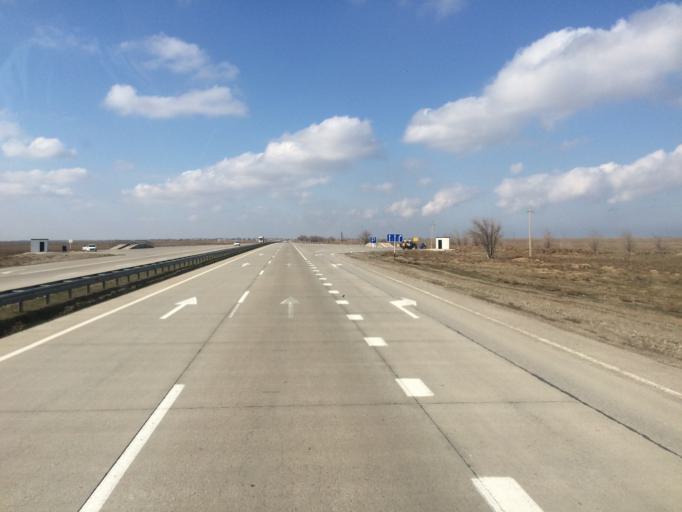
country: KZ
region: Ongtustik Qazaqstan
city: Temirlanovka
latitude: 42.8445
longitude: 69.0972
